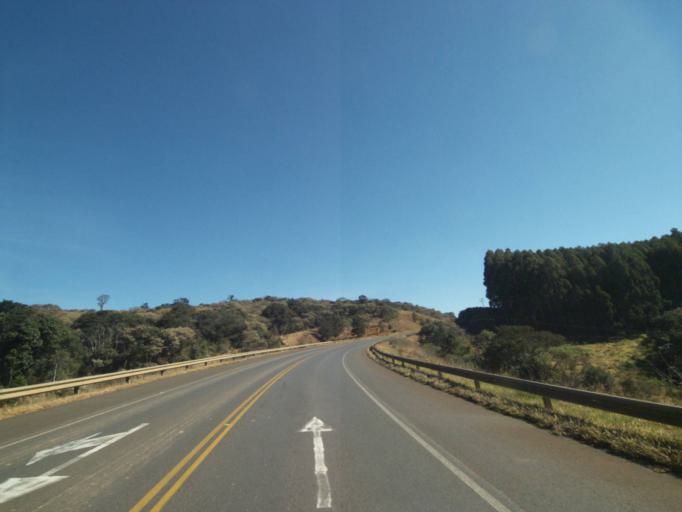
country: BR
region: Parana
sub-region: Tibagi
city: Tibagi
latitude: -24.4070
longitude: -50.3449
